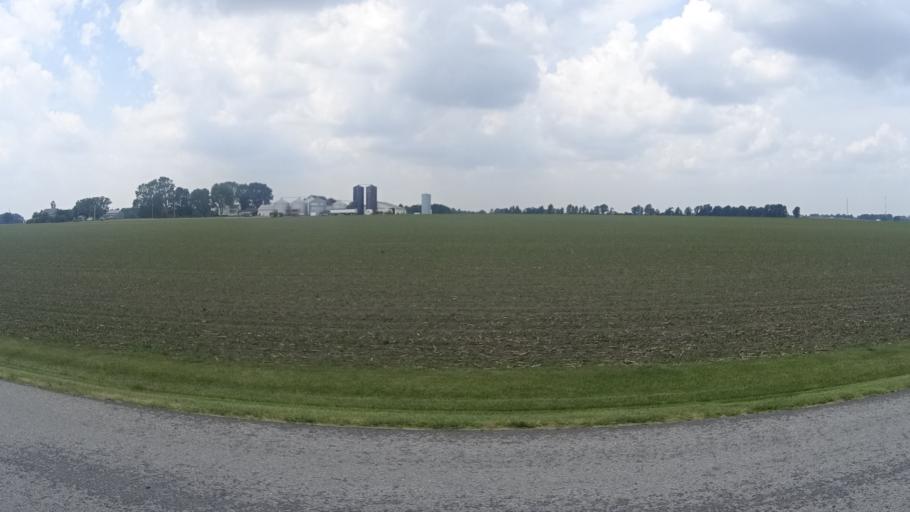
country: US
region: Ohio
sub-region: Erie County
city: Milan
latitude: 41.3247
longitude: -82.6736
